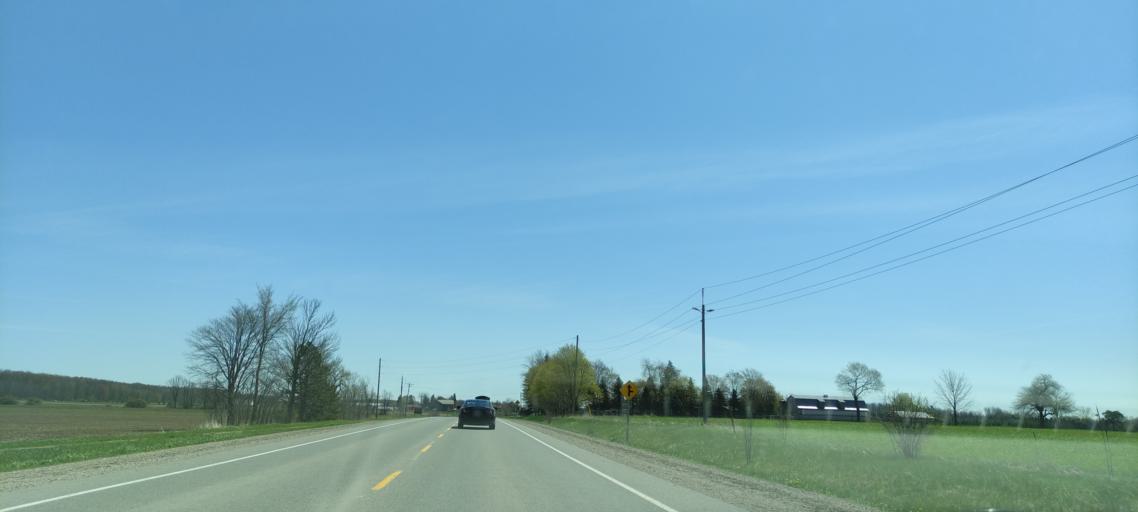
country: CA
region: Ontario
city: Waterloo
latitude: 43.5833
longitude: -80.4380
